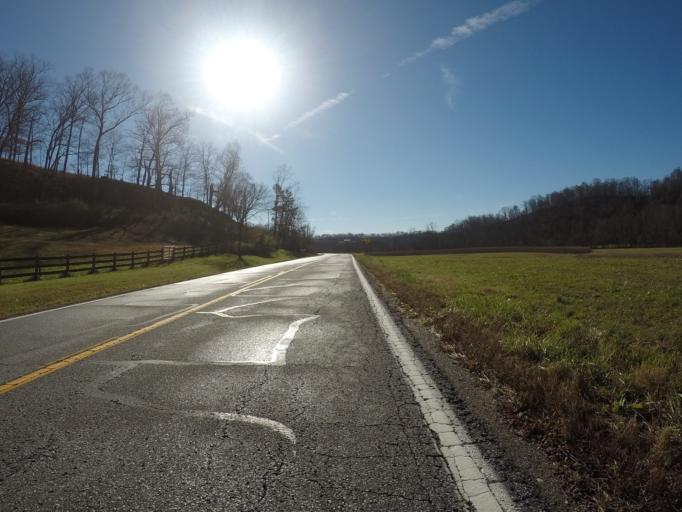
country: US
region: West Virginia
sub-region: Cabell County
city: Huntington
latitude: 38.4805
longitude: -82.4463
